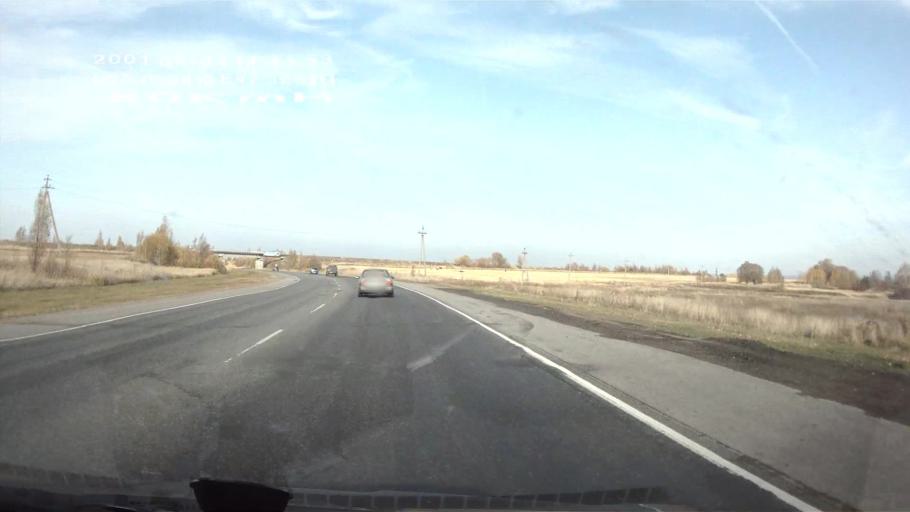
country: RU
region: Chuvashia
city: Kugesi
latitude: 56.0395
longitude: 47.3628
